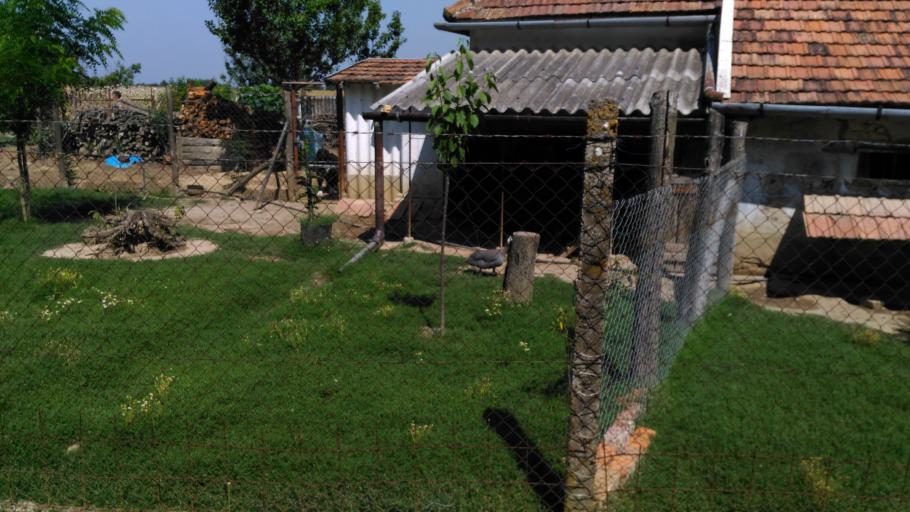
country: HU
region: Vas
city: Kormend
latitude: 46.9853
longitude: 16.6569
